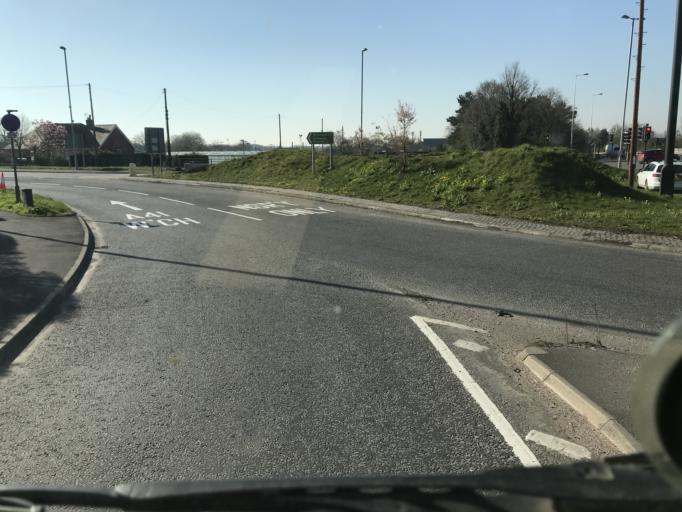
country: GB
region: England
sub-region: Cheshire West and Chester
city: Hoole
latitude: 53.1880
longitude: -2.8534
